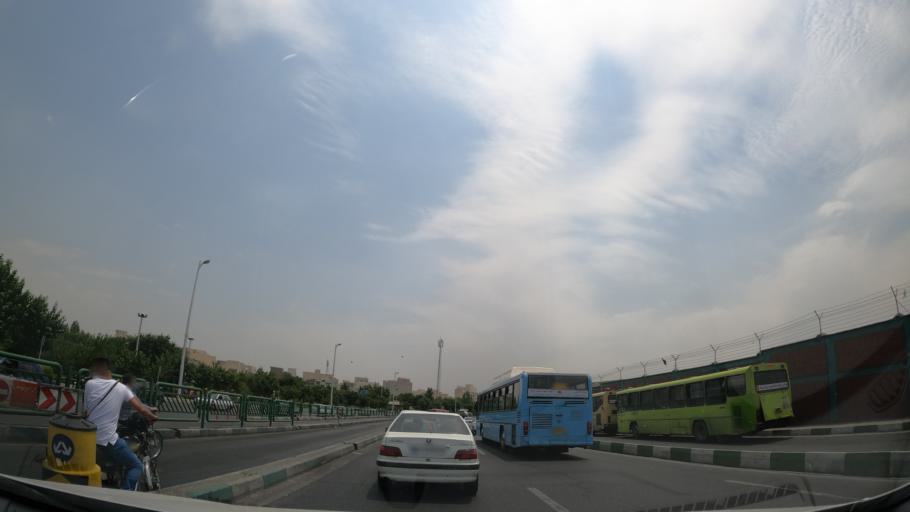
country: IR
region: Tehran
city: Tehran
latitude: 35.6963
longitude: 51.3390
